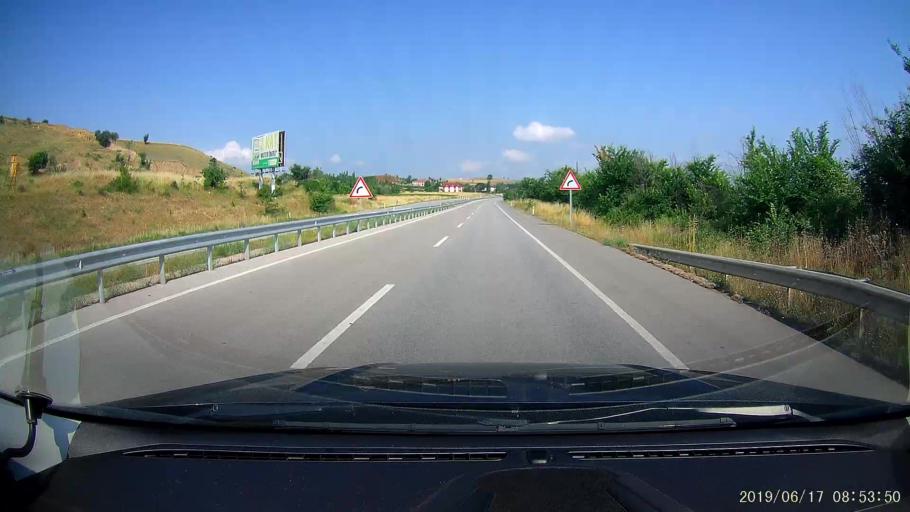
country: TR
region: Amasya
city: Esencay
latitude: 40.7133
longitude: 36.4732
